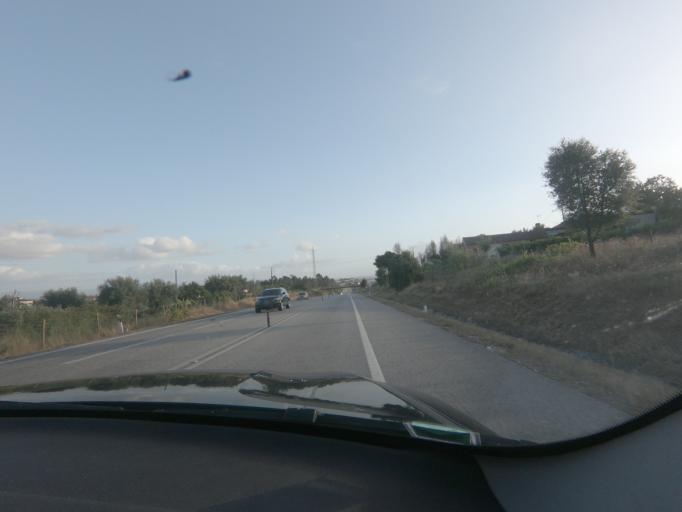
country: PT
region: Viseu
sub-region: Santa Comba Dao
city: Santa Comba Dao
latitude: 40.3705
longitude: -8.1289
